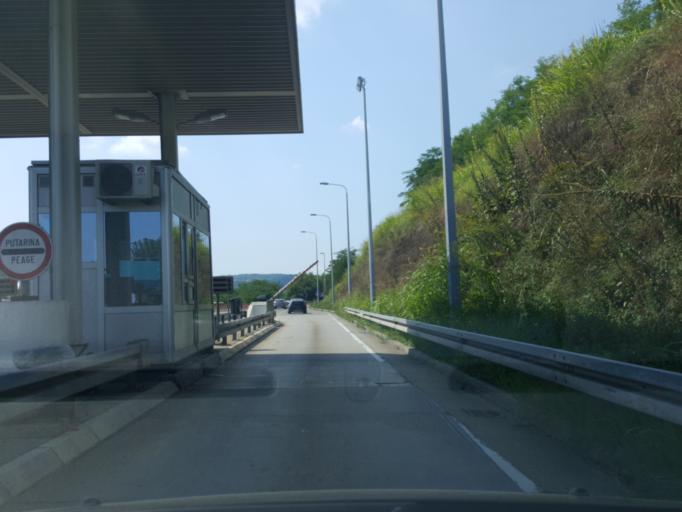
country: RS
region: Central Serbia
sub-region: Belgrade
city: Sopot
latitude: 44.5632
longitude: 20.6694
